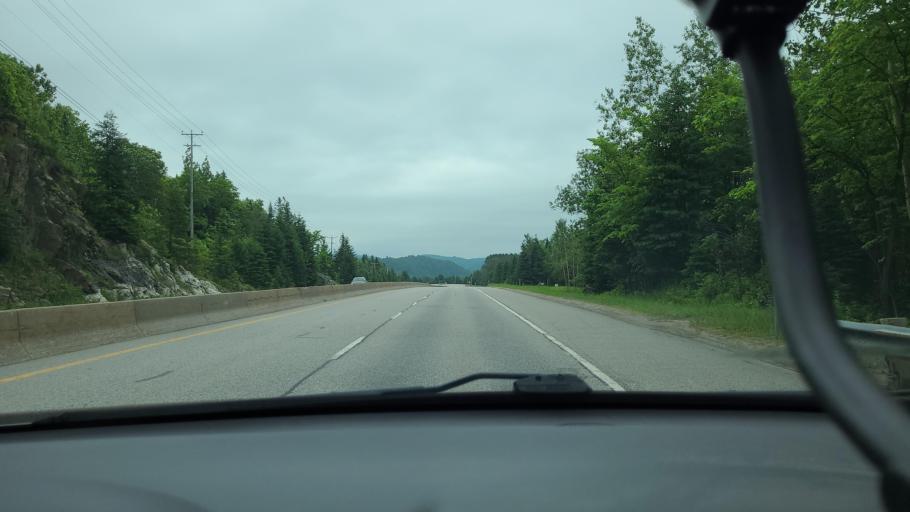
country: CA
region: Quebec
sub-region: Laurentides
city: Labelle
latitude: 46.1993
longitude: -74.7232
